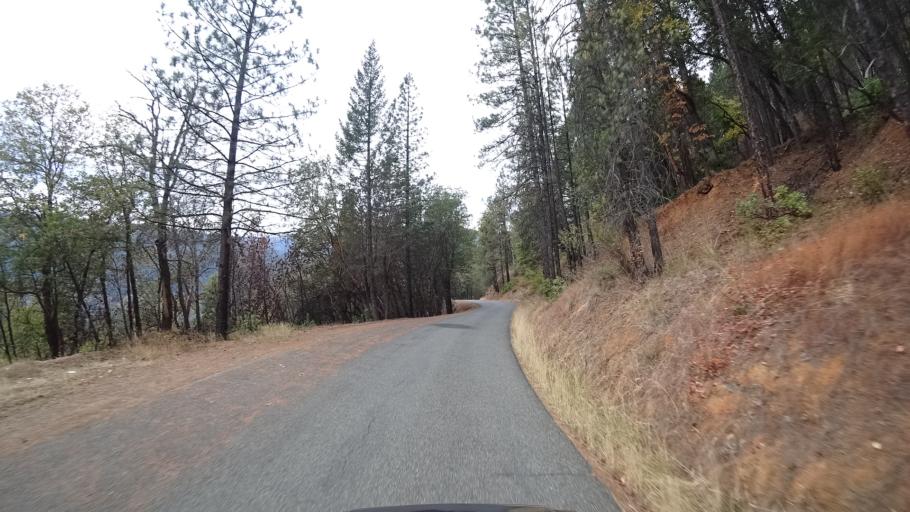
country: US
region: California
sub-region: Siskiyou County
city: Happy Camp
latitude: 41.7794
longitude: -123.3843
